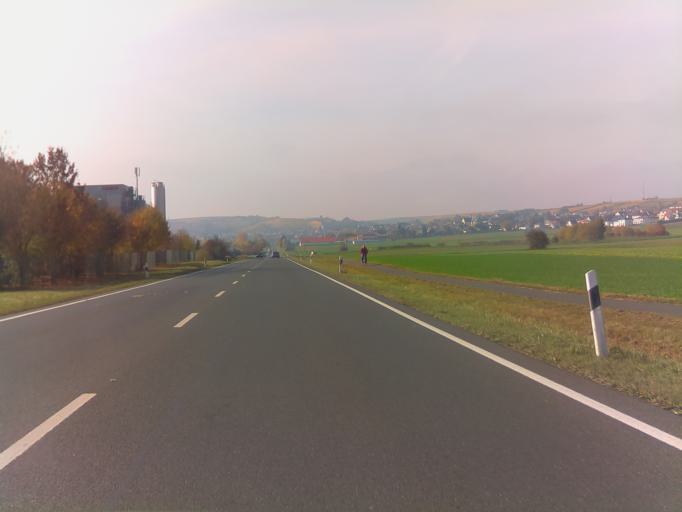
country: DE
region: Bavaria
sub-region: Regierungsbezirk Unterfranken
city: Sommerach
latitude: 49.8035
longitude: 10.1981
